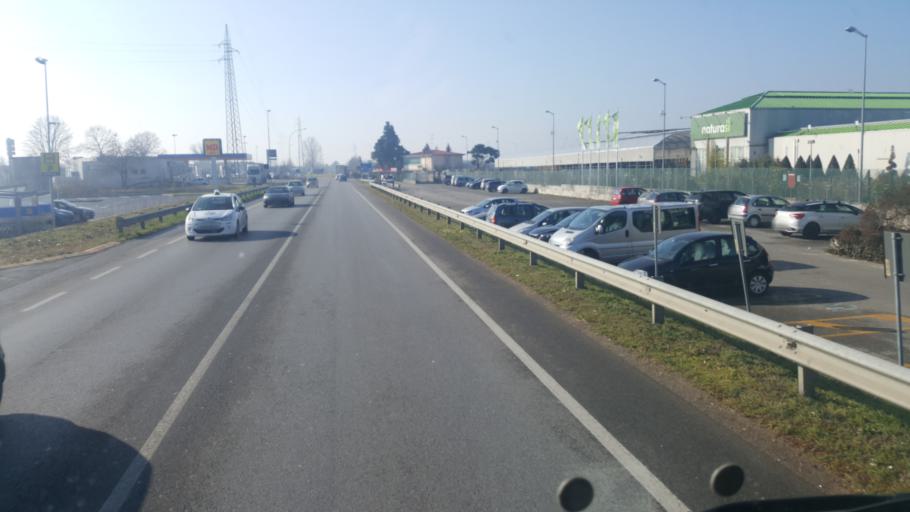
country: IT
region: Lombardy
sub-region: Citta metropolitana di Milano
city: Magenta
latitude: 45.4693
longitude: 8.8657
